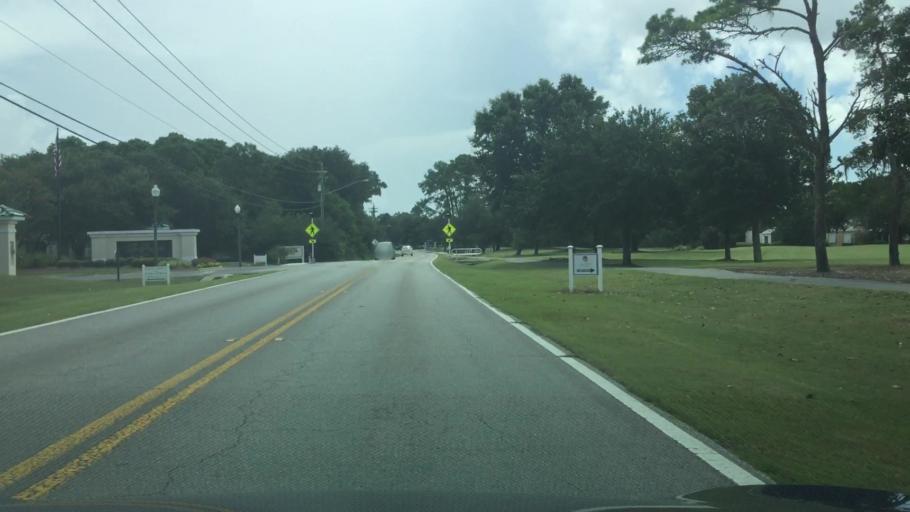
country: US
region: Florida
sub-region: Bay County
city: Upper Grand Lagoon
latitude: 30.1527
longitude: -85.7261
